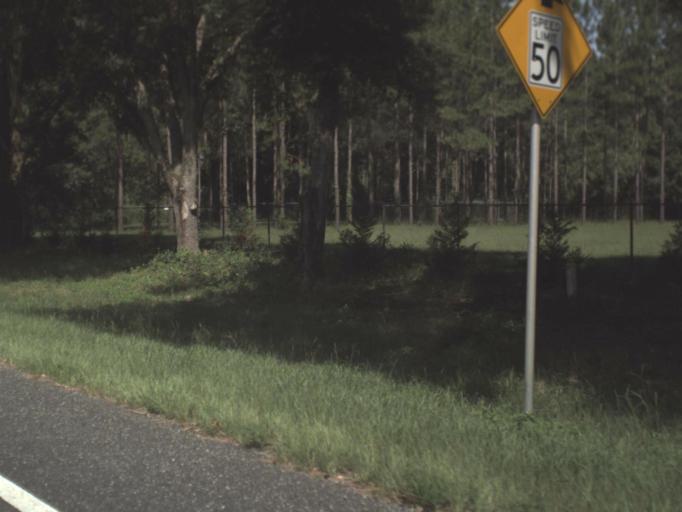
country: US
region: Florida
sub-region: Levy County
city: Chiefland
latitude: 29.4938
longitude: -82.8491
